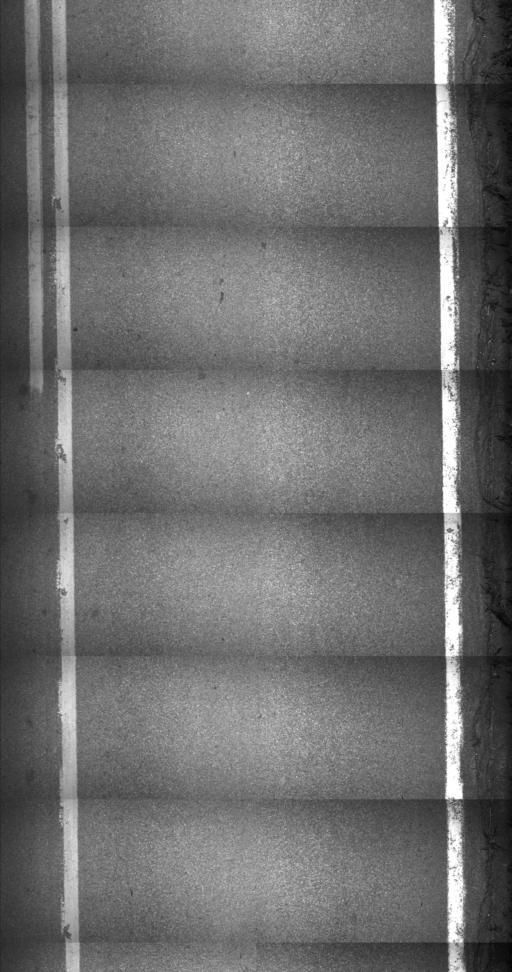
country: US
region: Vermont
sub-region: Rutland County
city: Brandon
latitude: 43.7904
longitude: -73.2042
